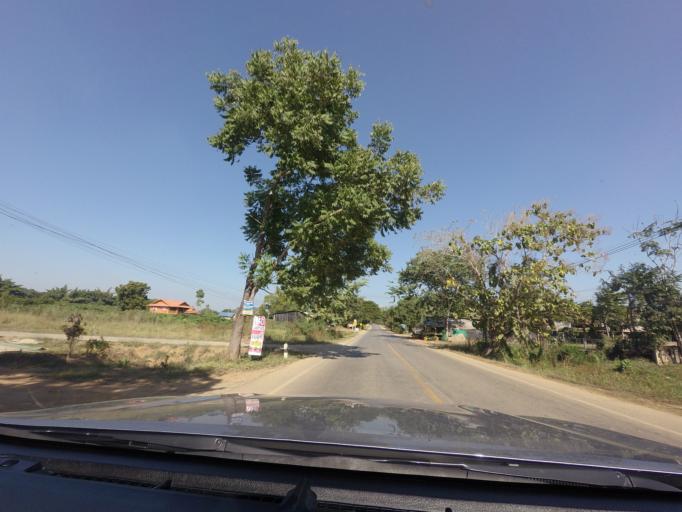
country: TH
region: Sukhothai
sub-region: Amphoe Si Satchanalai
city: Si Satchanalai
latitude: 17.6849
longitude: 99.7072
